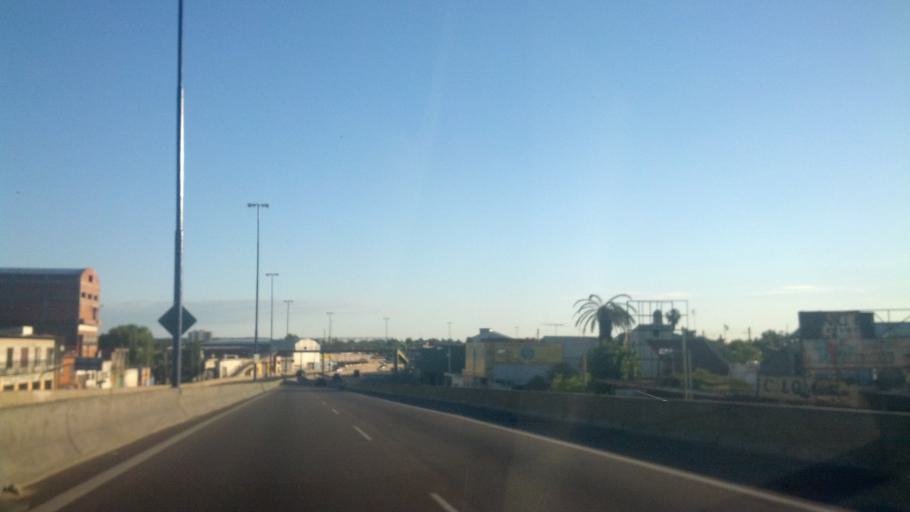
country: AR
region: Buenos Aires
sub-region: Partido de Lomas de Zamora
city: Lomas de Zamora
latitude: -34.7458
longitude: -58.4299
